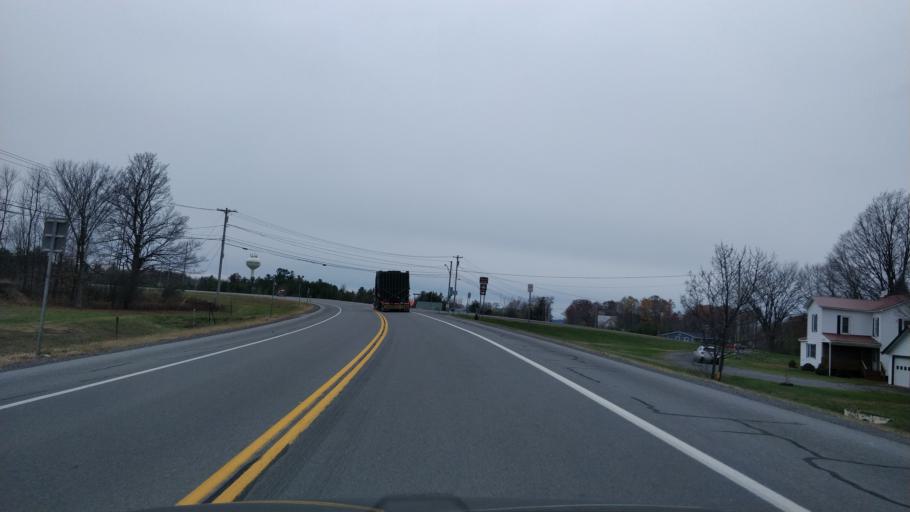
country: CA
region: Ontario
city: Brockville
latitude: 44.5934
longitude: -75.6376
